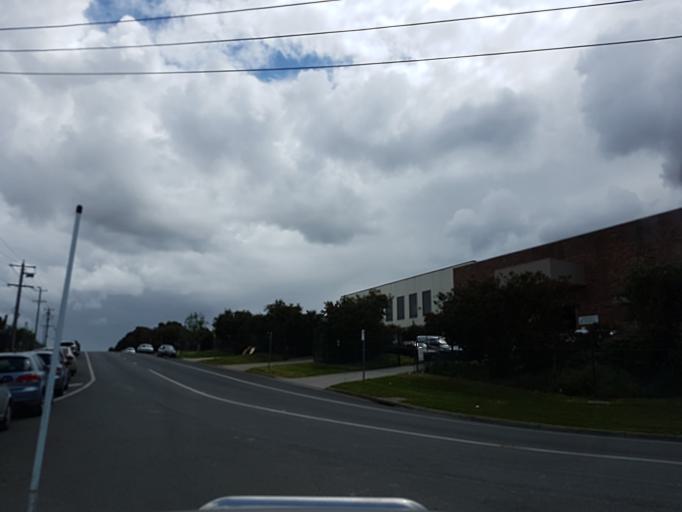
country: AU
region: Victoria
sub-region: Casey
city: Hallam
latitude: -38.0166
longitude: 145.2689
